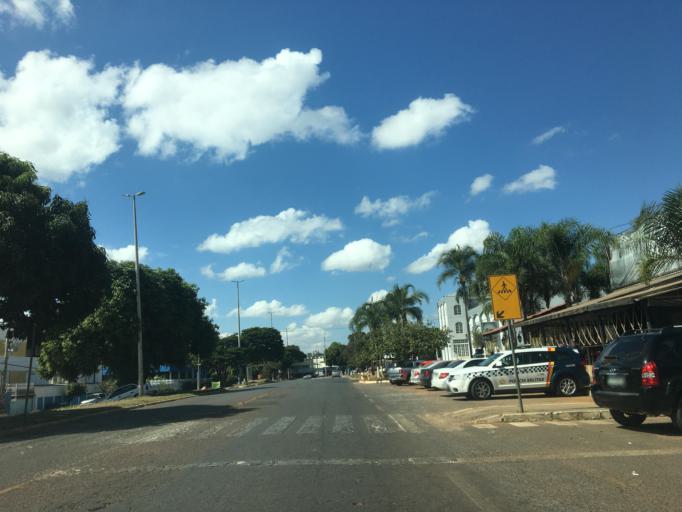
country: BR
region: Federal District
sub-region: Brasilia
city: Brasilia
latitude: -15.6459
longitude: -47.7887
